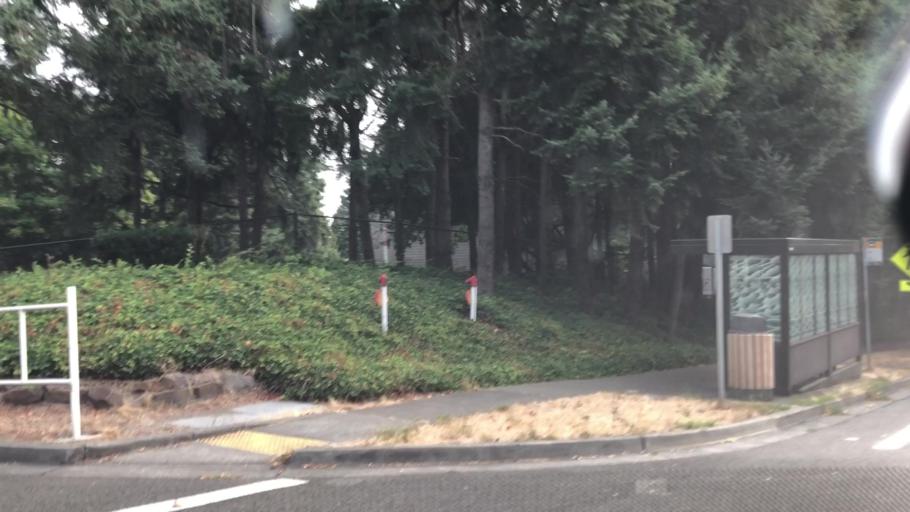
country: US
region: Washington
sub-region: King County
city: Redmond
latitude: 47.6670
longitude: -122.1585
